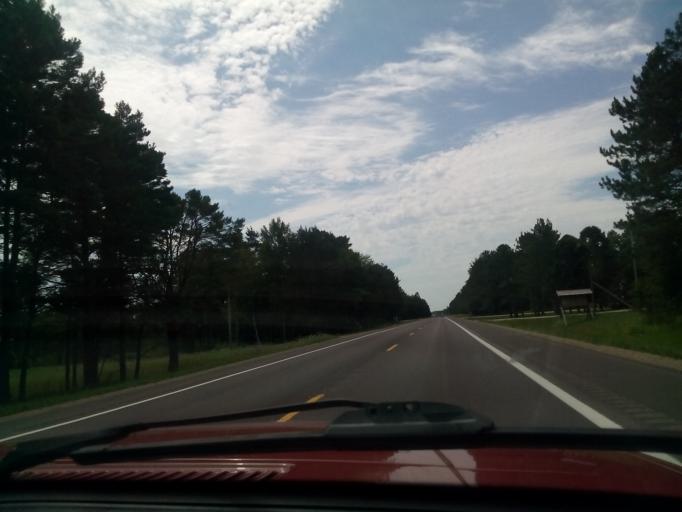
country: US
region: Michigan
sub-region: Schoolcraft County
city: Manistique
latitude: 46.0501
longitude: -85.9658
